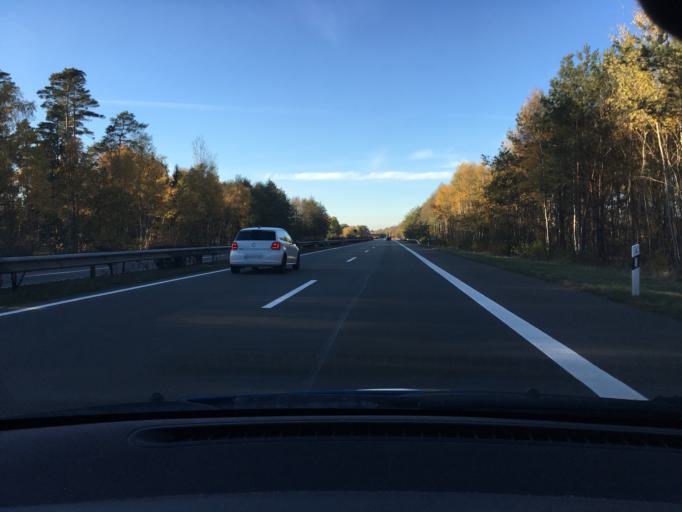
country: DE
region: Lower Saxony
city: Radbruch
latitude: 53.3185
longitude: 10.3100
